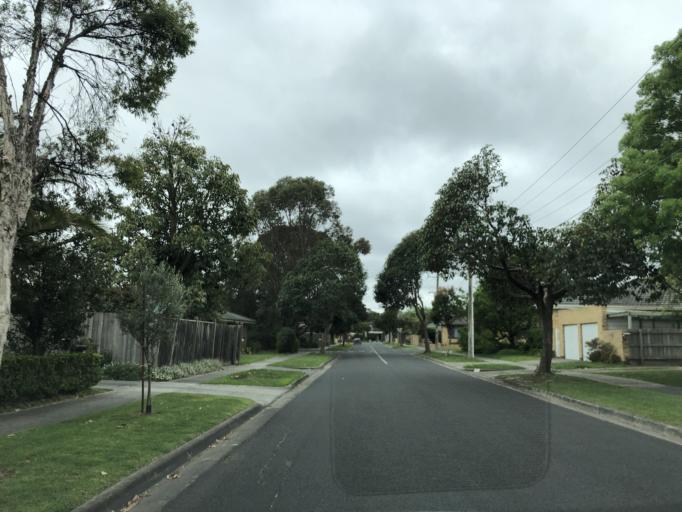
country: AU
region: Victoria
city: Burwood East
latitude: -37.8629
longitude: 145.1478
